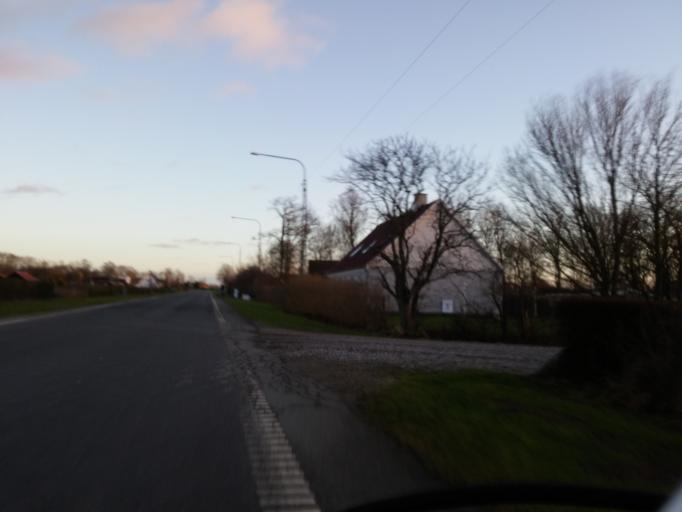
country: DK
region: South Denmark
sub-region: Kerteminde Kommune
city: Munkebo
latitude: 55.4634
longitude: 10.5455
